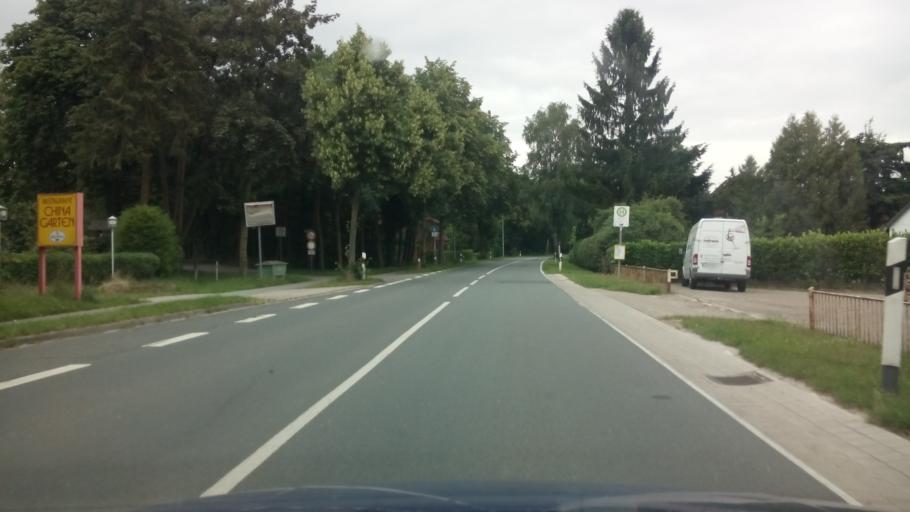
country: DE
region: Lower Saxony
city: Worpswede
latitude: 53.2082
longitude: 8.9302
